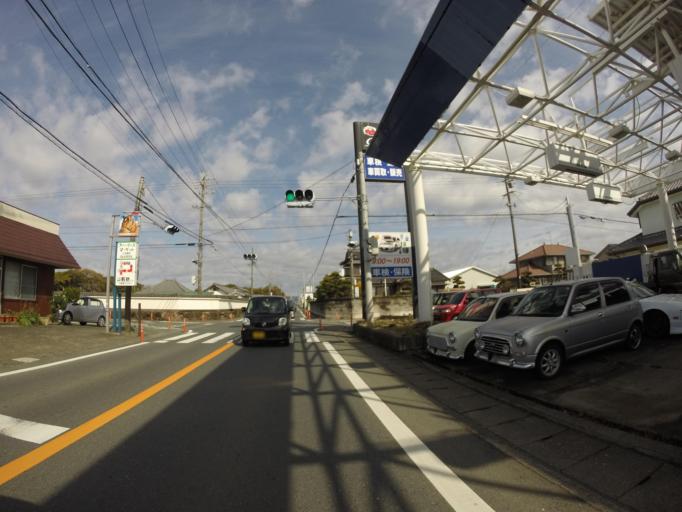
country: JP
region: Shizuoka
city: Hamakita
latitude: 34.7913
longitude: 137.7035
